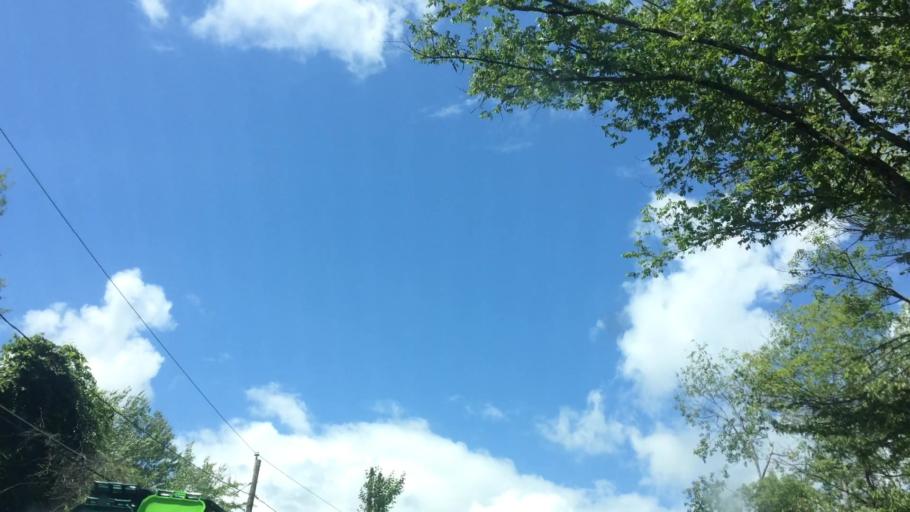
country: US
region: Massachusetts
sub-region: Middlesex County
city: Sudbury
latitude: 42.3766
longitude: -71.3981
